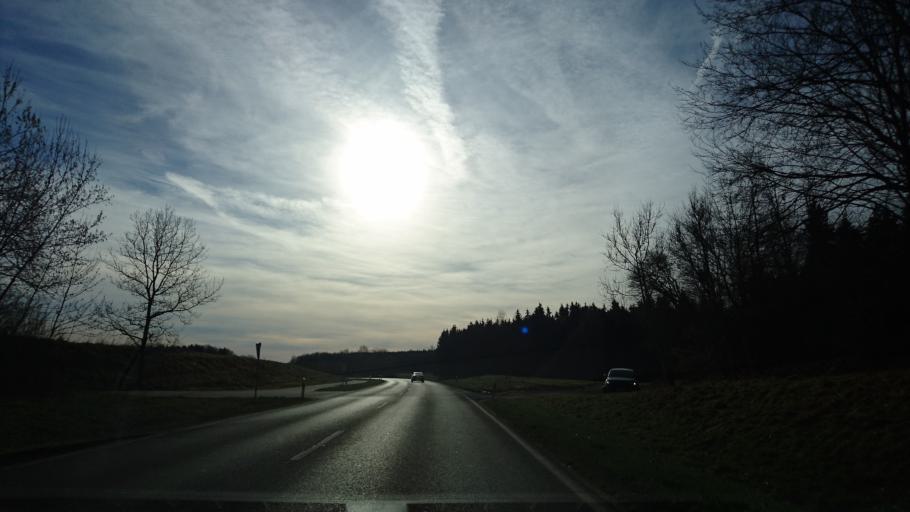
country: DE
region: Bavaria
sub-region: Swabia
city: Biberbach
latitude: 48.5267
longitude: 10.7783
